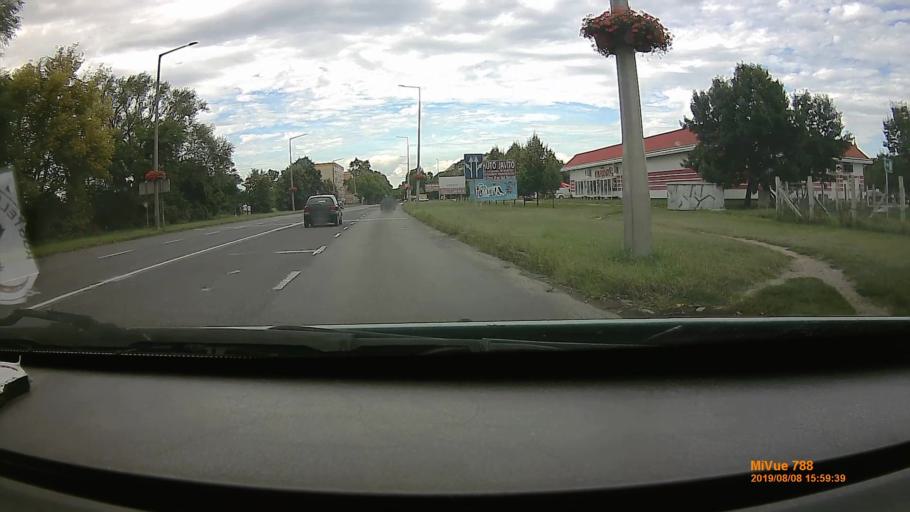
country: HU
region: Szabolcs-Szatmar-Bereg
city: Mateszalka
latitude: 47.9489
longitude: 22.3250
